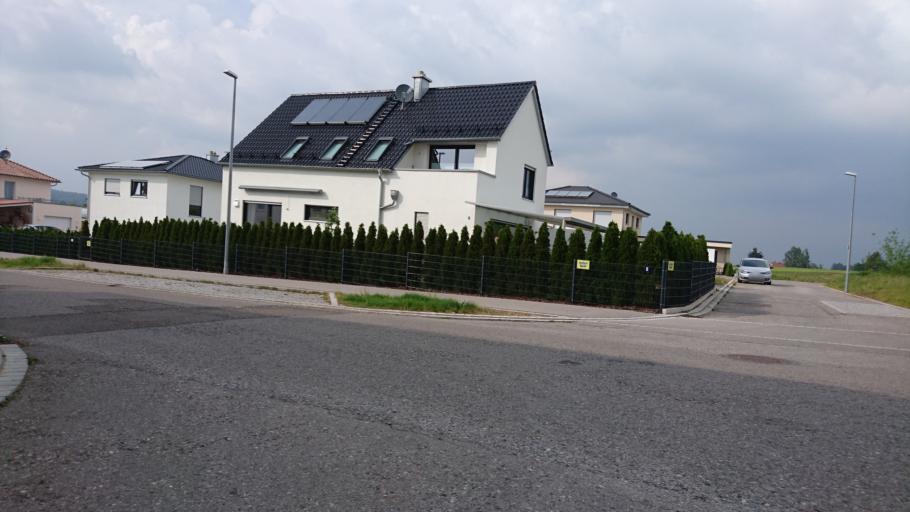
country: DE
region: Bavaria
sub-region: Swabia
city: Diedorf
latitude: 48.3584
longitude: 10.7876
